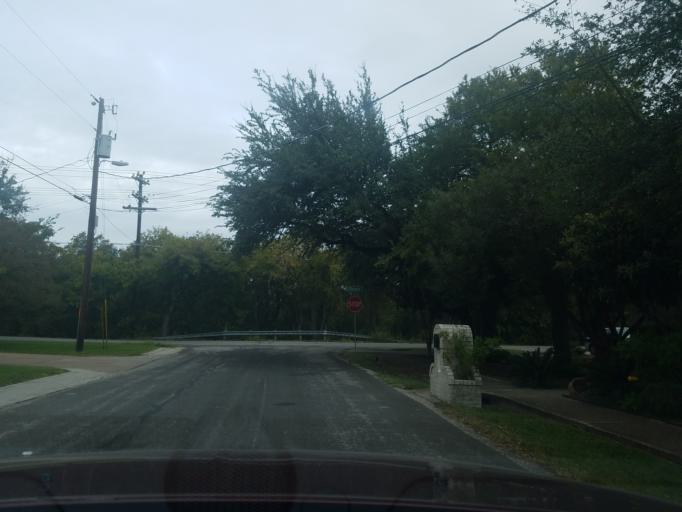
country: US
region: Texas
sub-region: Williamson County
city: Cedar Park
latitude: 30.4813
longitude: -97.8094
